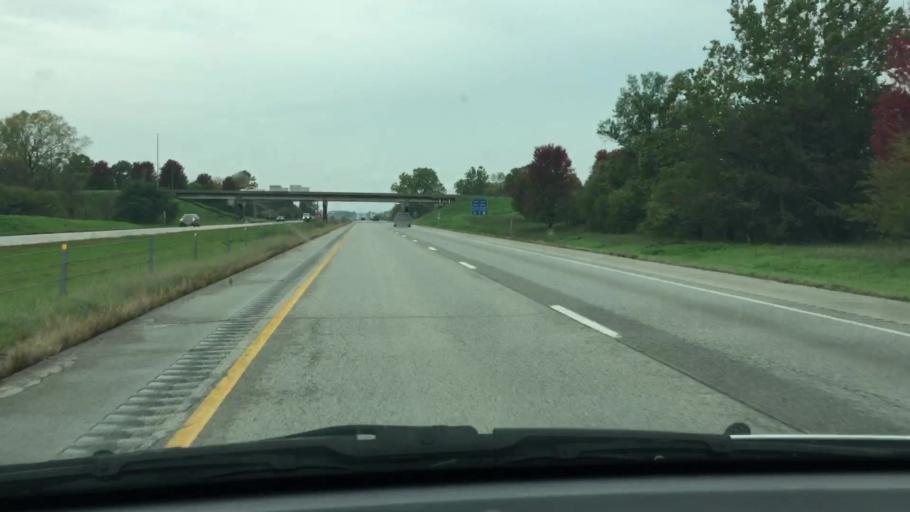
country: US
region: Iowa
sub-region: Johnson County
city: Tiffin
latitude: 41.6940
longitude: -91.6640
